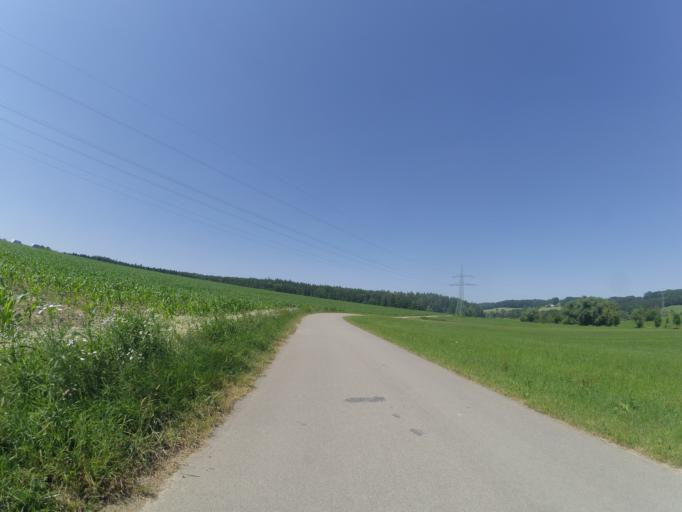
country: DE
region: Bavaria
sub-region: Swabia
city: Ottobeuren
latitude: 47.9512
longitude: 10.2904
